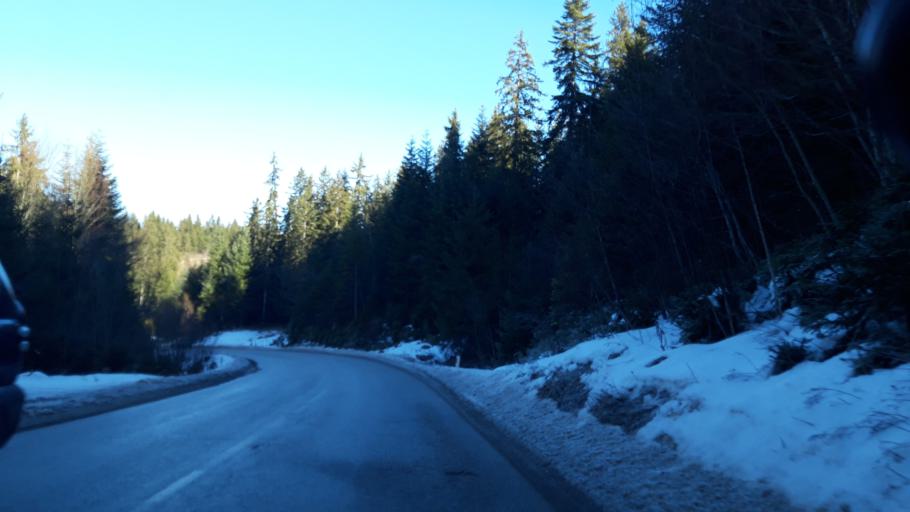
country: BA
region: Republika Srpska
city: Koran
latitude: 43.7863
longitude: 18.5532
